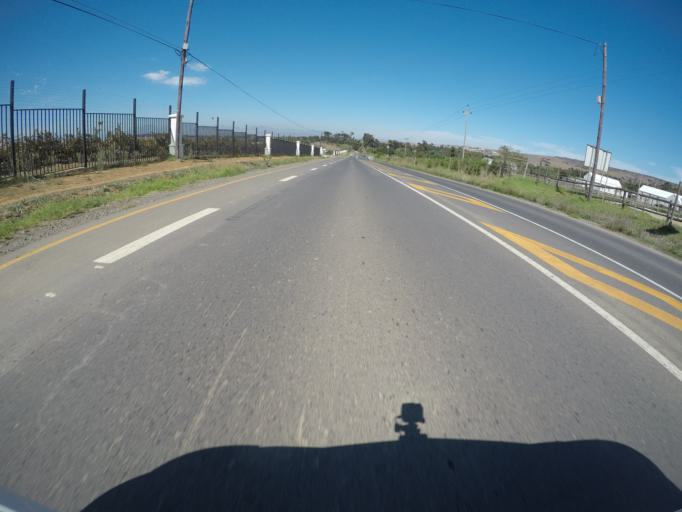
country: ZA
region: Western Cape
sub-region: City of Cape Town
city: Kraaifontein
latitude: -33.8068
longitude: 18.6229
